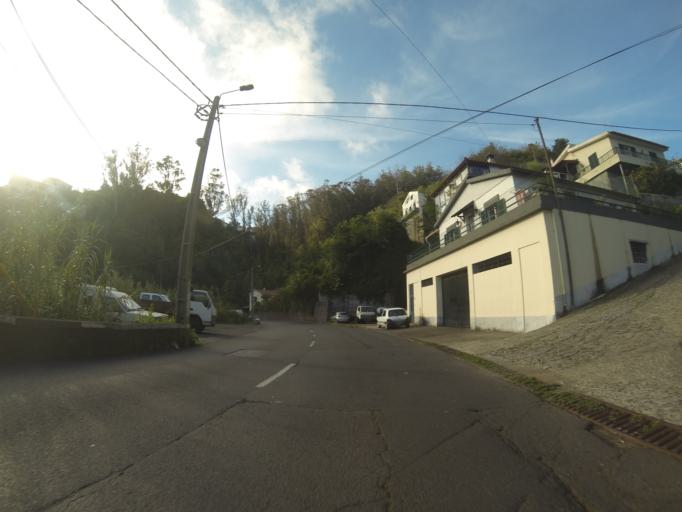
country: PT
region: Madeira
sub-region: Funchal
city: Nossa Senhora do Monte
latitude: 32.6610
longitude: -16.8836
